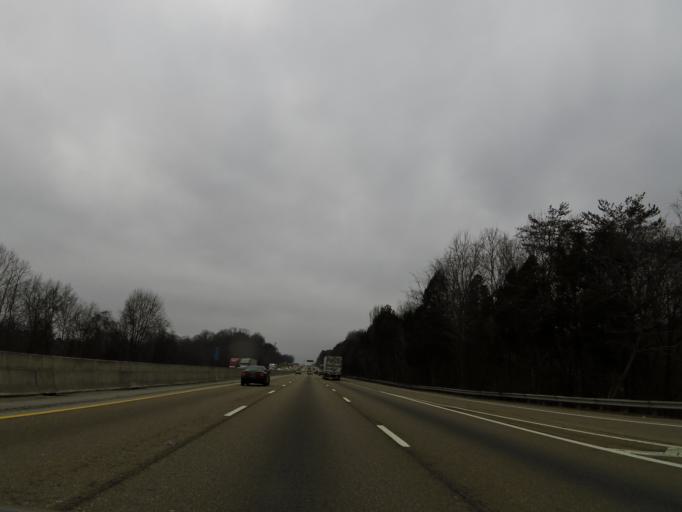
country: US
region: Tennessee
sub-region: Knox County
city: Farragut
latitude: 35.8984
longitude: -84.1769
